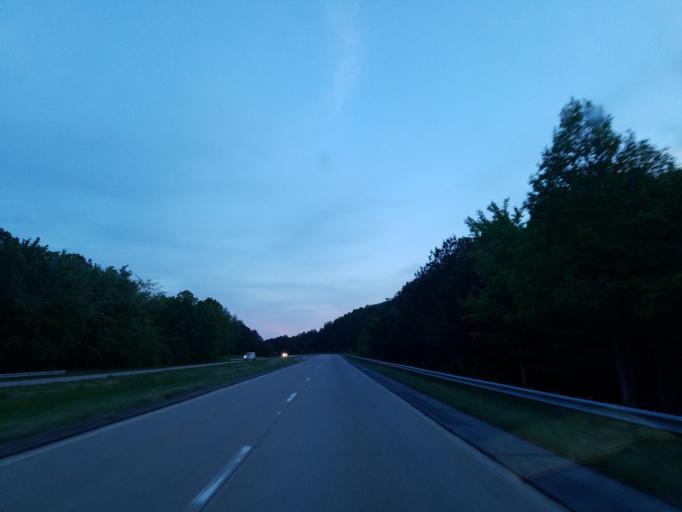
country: US
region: Georgia
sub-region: Gilmer County
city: Ellijay
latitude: 34.5807
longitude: -84.5189
